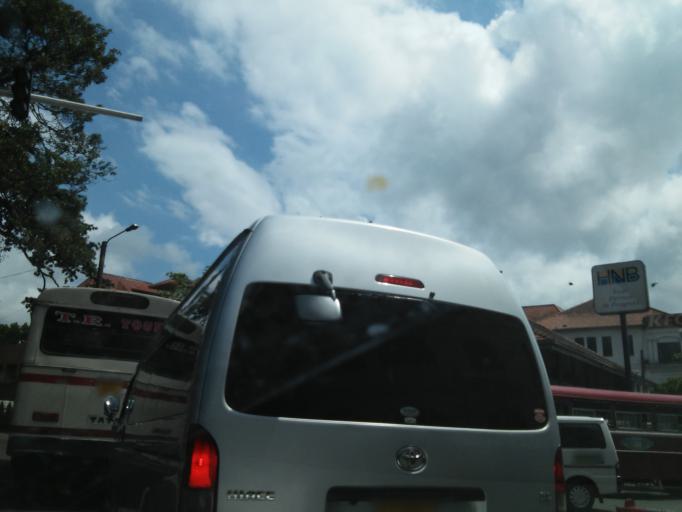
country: LK
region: Central
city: Kandy
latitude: 7.2930
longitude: 80.6378
